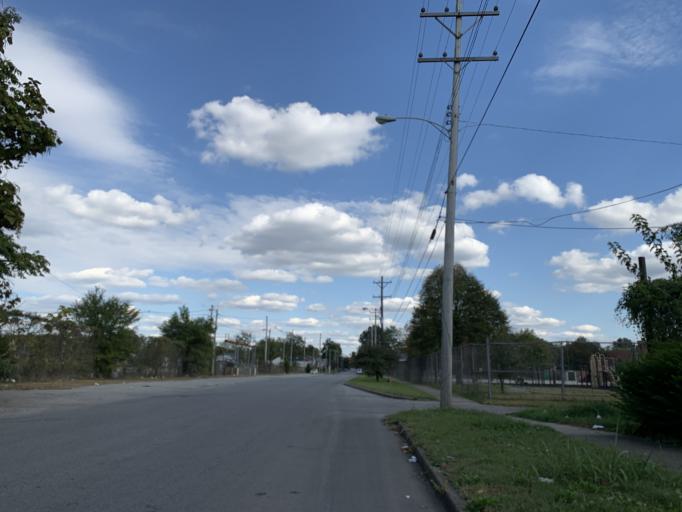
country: US
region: Kentucky
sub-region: Jefferson County
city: Louisville
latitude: 38.2451
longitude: -85.8015
